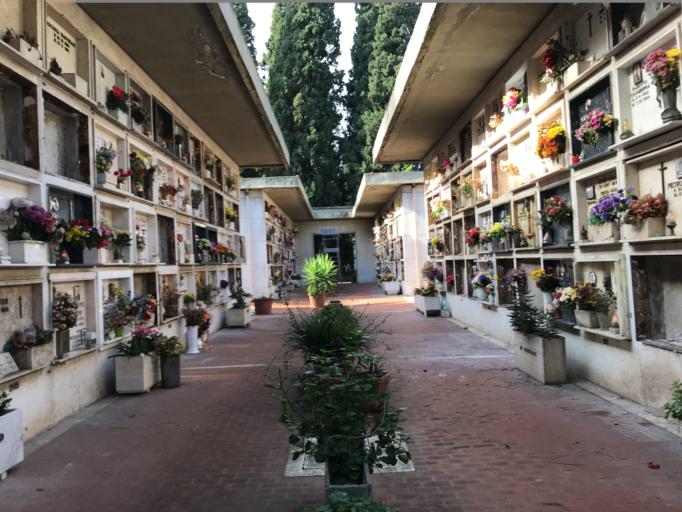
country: IT
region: Latium
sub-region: Citta metropolitana di Roma Capitale
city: Rome
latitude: 41.9067
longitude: 12.5319
